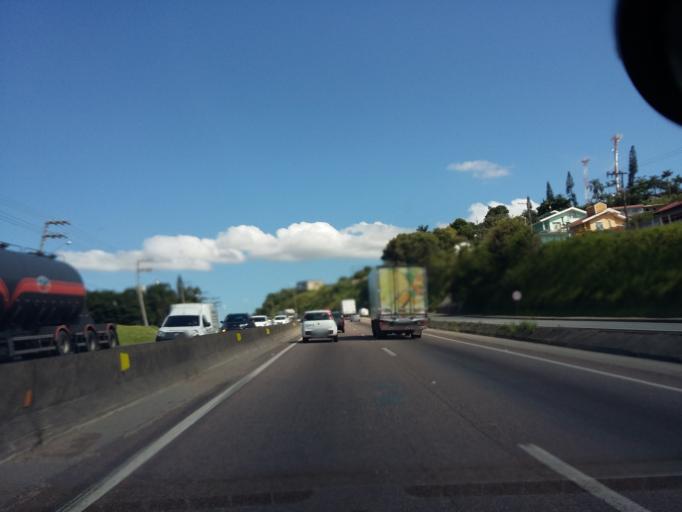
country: BR
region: Santa Catarina
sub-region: Biguacu
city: Biguacu
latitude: -27.5157
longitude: -48.6394
